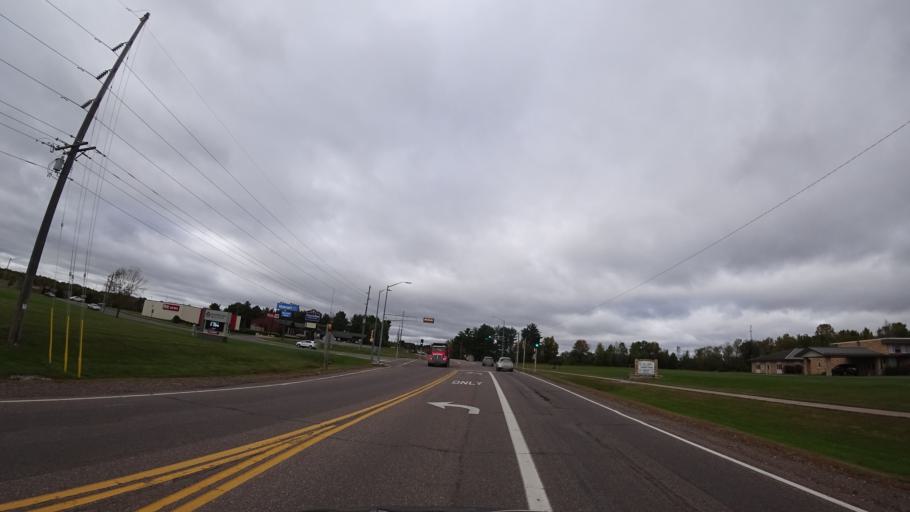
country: US
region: Wisconsin
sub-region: Rusk County
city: Ladysmith
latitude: 45.4563
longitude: -91.1088
